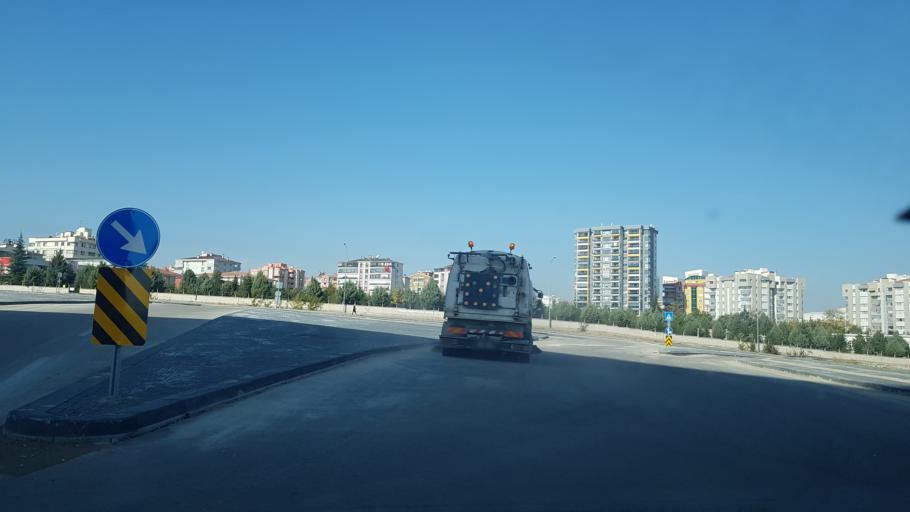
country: TR
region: Ankara
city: Etimesgut
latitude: 39.9725
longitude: 32.6122
